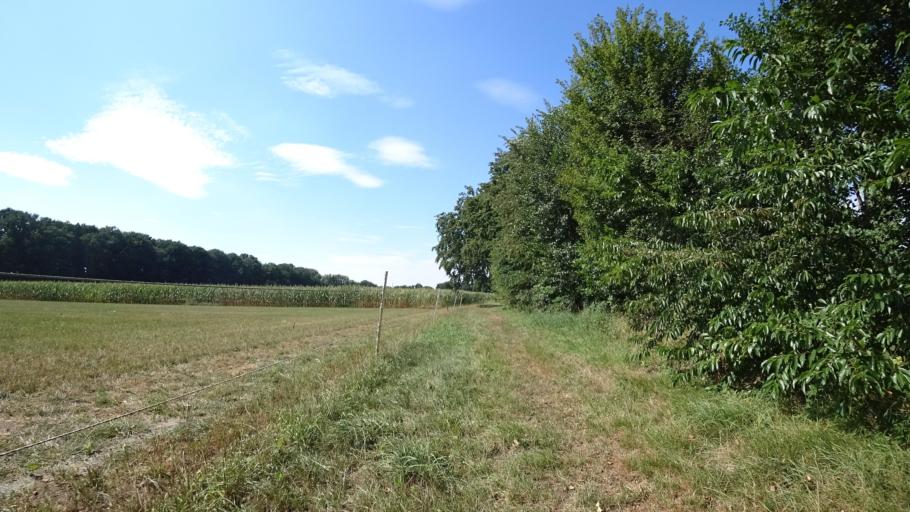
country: DE
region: North Rhine-Westphalia
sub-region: Regierungsbezirk Detmold
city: Guetersloh
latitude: 51.9435
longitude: 8.3955
